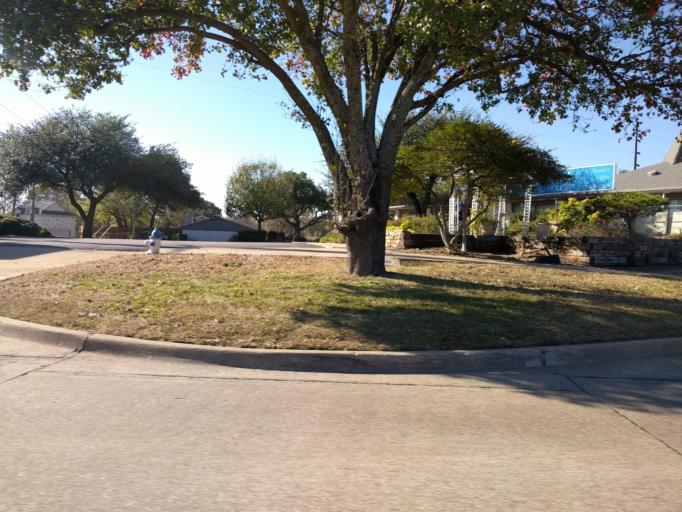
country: US
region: Texas
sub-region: Dallas County
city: Richardson
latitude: 32.9760
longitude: -96.7364
